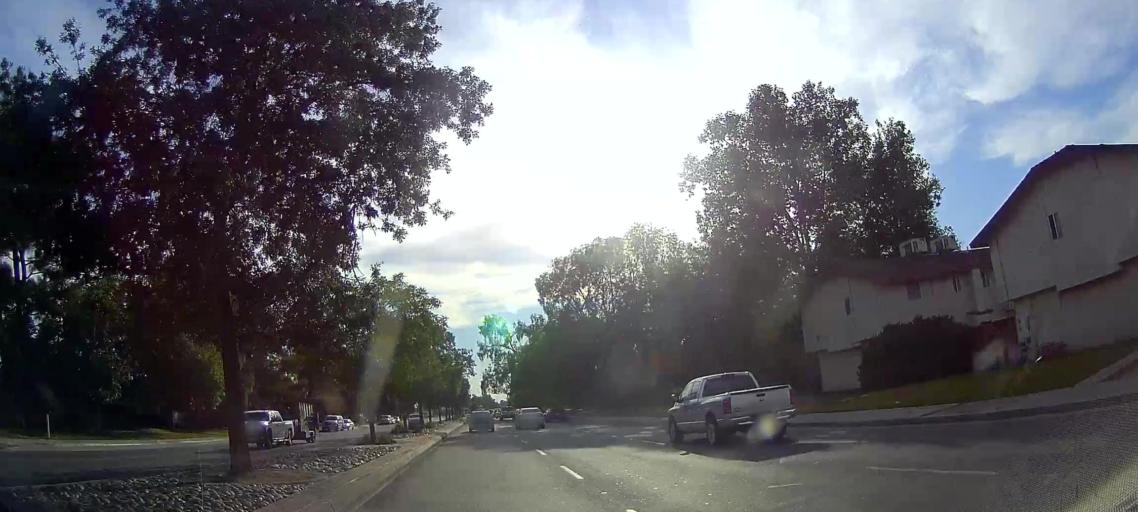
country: US
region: California
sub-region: Kern County
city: Bakersfield
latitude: 35.3178
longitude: -119.0494
